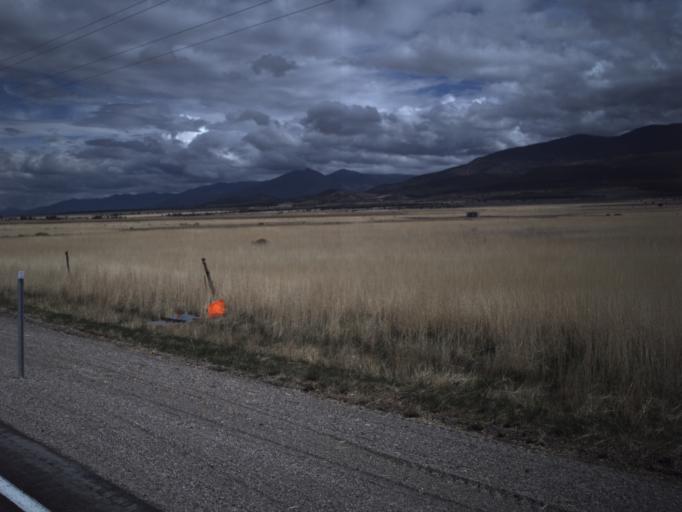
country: US
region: Utah
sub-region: Millard County
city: Fillmore
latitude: 38.8525
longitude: -112.4218
